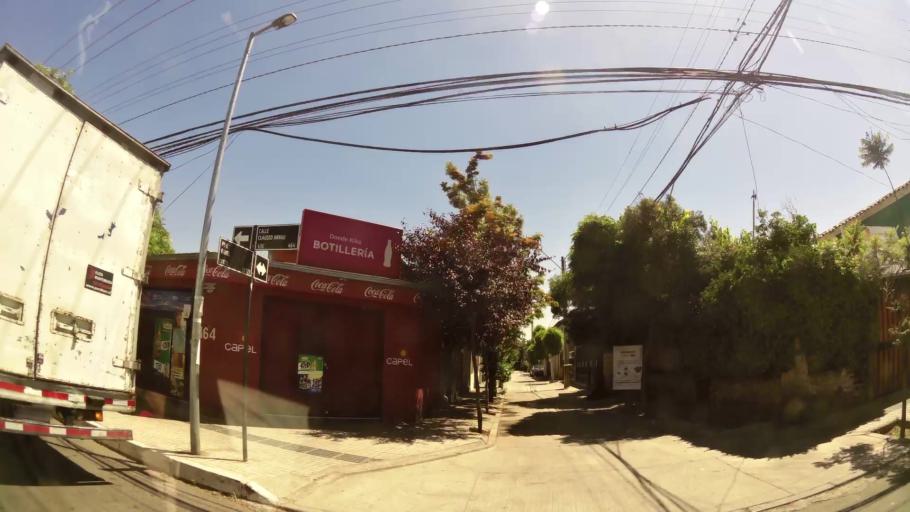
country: CL
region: Santiago Metropolitan
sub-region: Provincia de Maipo
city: San Bernardo
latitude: -33.5653
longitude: -70.6782
